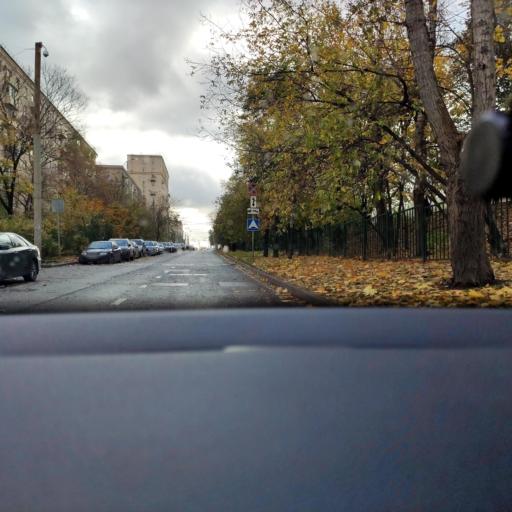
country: RU
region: Moskovskaya
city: Kastanayevo
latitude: 55.7399
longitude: 37.5146
